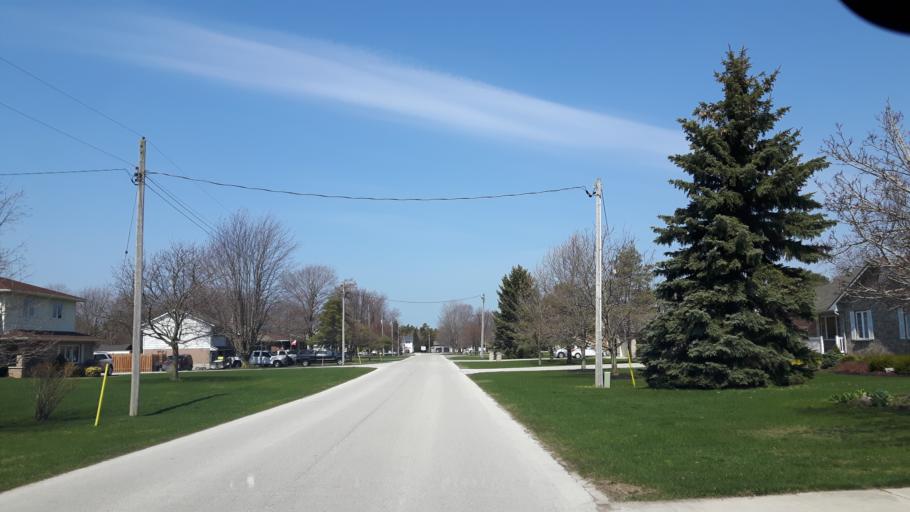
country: CA
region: Ontario
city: Goderich
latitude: 43.7248
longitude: -81.6841
